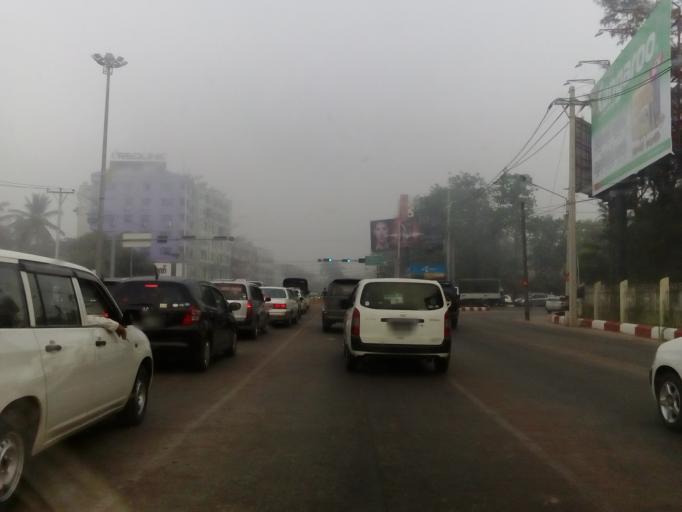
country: MM
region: Yangon
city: Yangon
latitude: 16.8217
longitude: 96.1829
